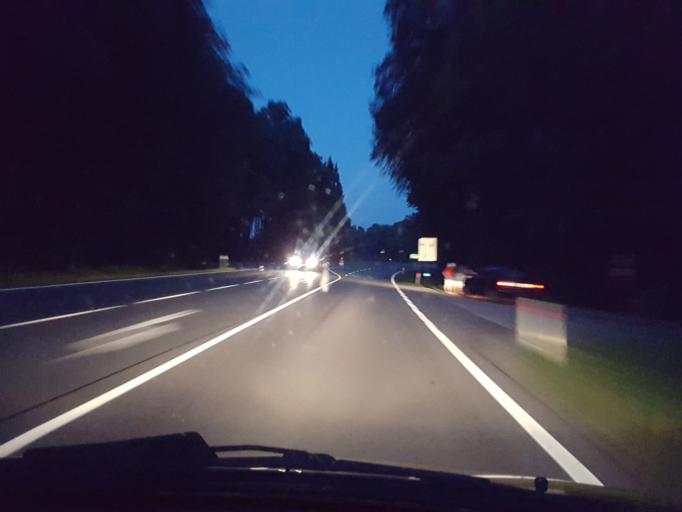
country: AT
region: Lower Austria
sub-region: Politischer Bezirk Scheibbs
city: Wieselburg
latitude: 48.1497
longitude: 15.1265
